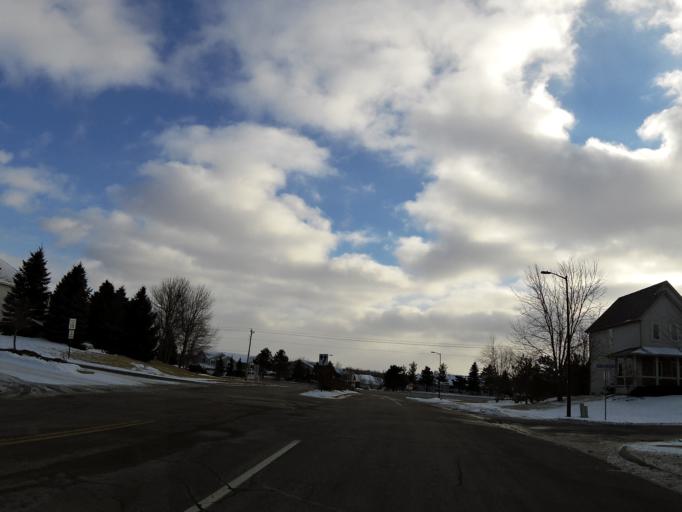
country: US
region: Minnesota
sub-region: Scott County
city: Prior Lake
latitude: 44.7259
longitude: -93.4508
